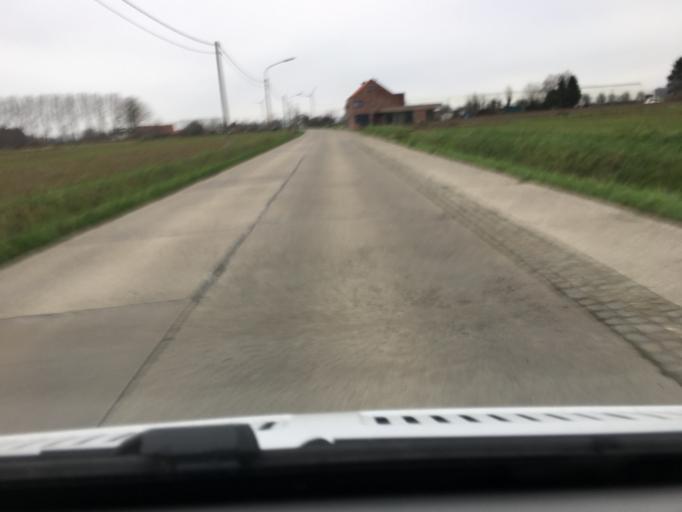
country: FR
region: Nord-Pas-de-Calais
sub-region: Departement du Nord
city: Bousbecque
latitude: 50.7806
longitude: 3.0759
